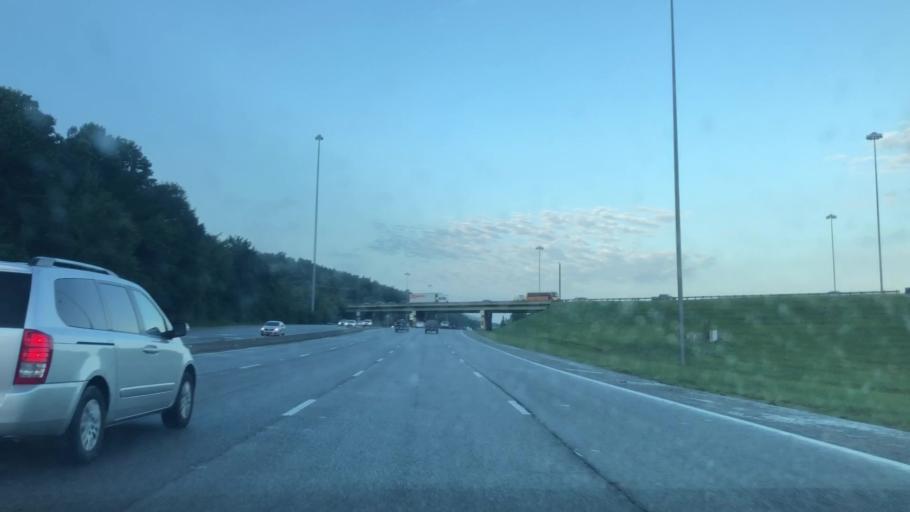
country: US
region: Alabama
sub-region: Shelby County
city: Indian Springs Village
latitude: 33.3558
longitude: -86.7774
